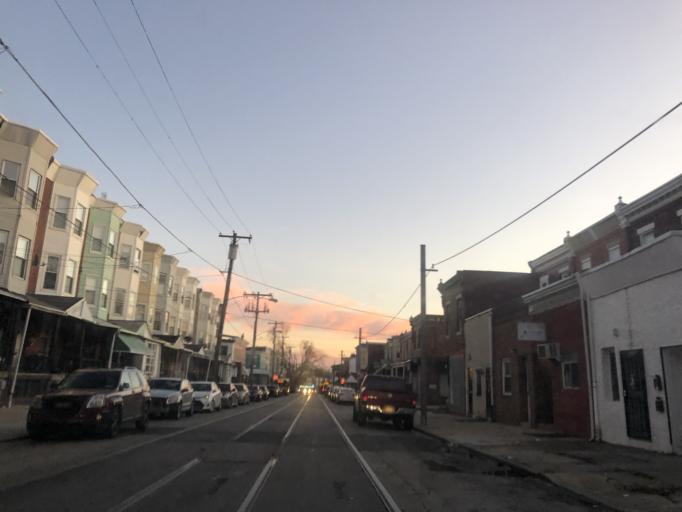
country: US
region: Pennsylvania
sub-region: Delaware County
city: Millbourne
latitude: 39.9721
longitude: -75.2392
